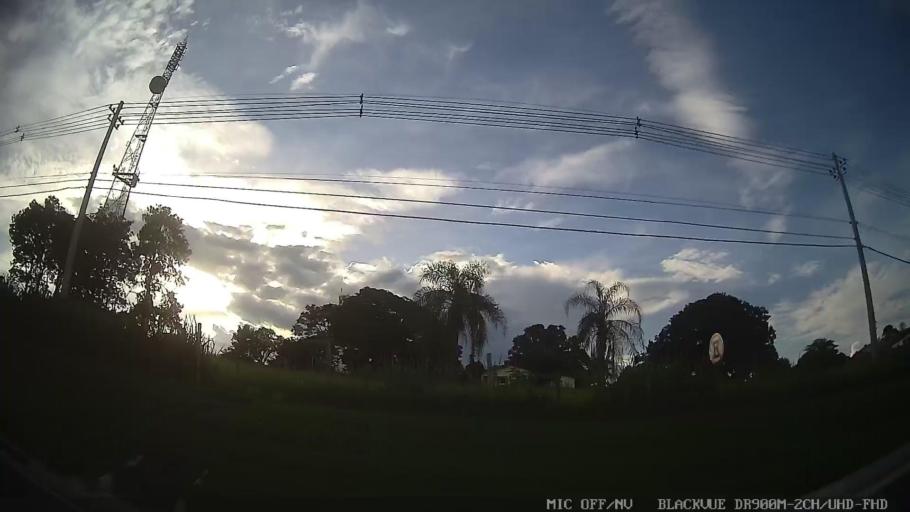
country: BR
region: Sao Paulo
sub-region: Tiete
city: Tiete
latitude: -23.0662
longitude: -47.7294
